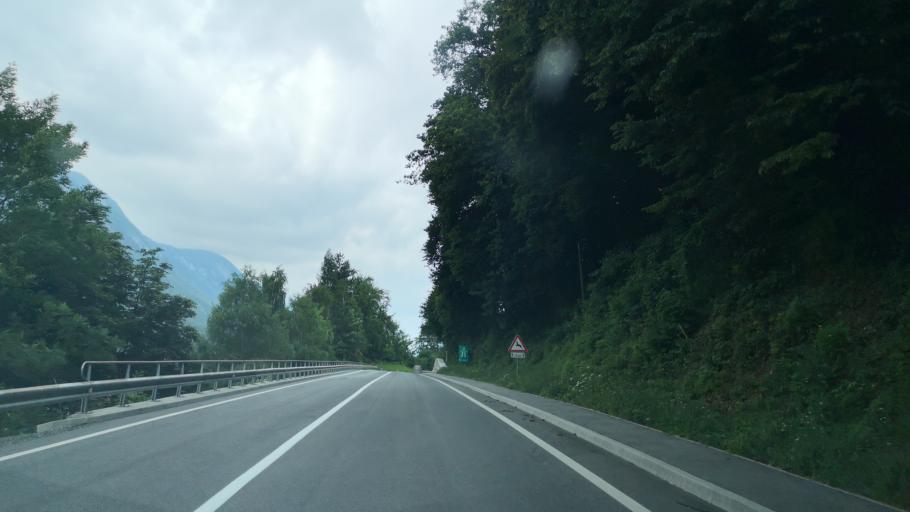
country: SI
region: Jesenice
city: Hrusica
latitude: 46.4435
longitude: 14.0339
